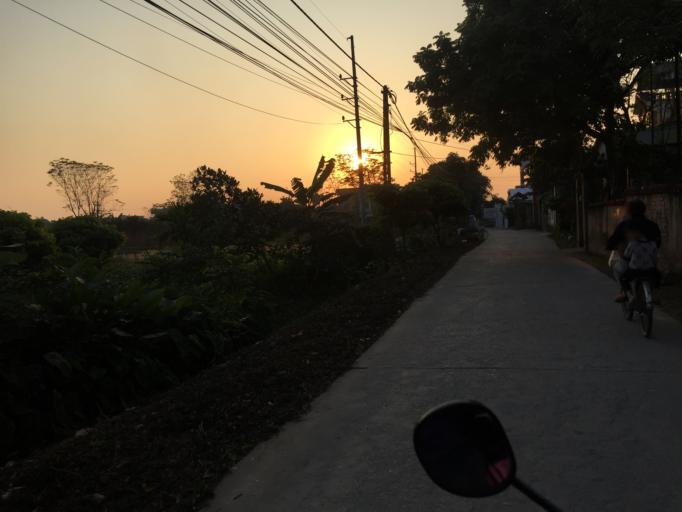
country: VN
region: Ha Noi
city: Chuc Son
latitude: 20.9036
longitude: 105.7225
